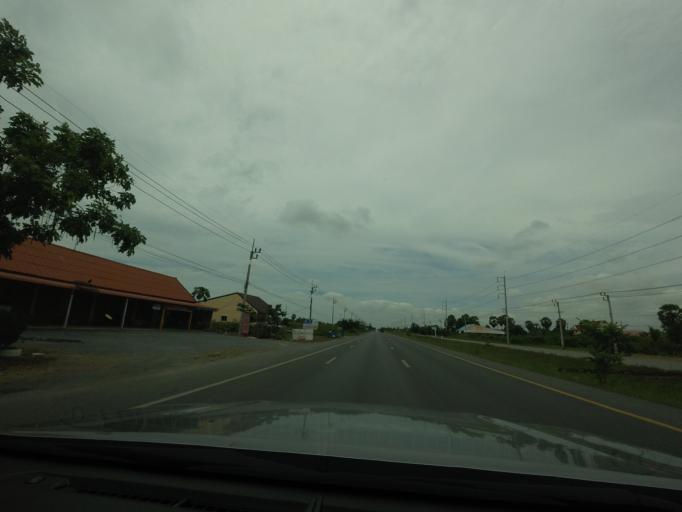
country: TH
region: Nakhon Si Thammarat
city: Hua Sai
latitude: 8.0376
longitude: 100.2887
